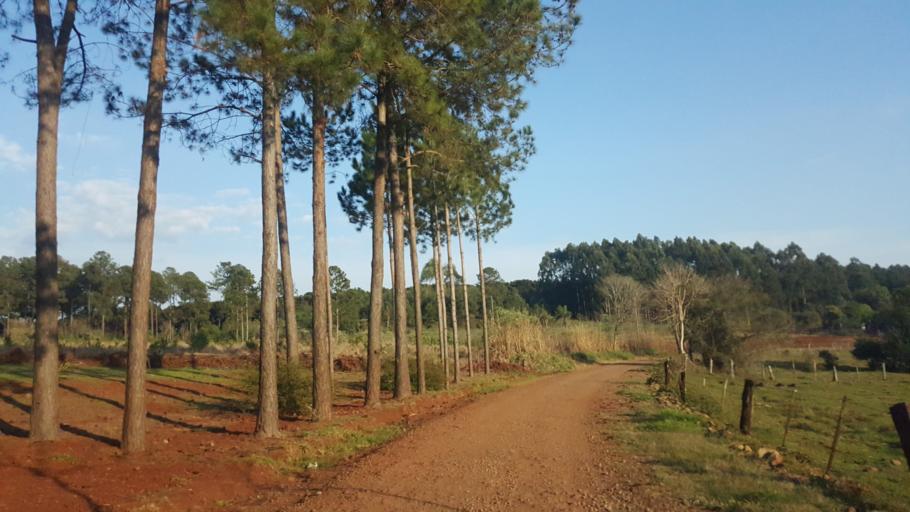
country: AR
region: Misiones
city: Capiovi
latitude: -26.9029
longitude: -55.0533
